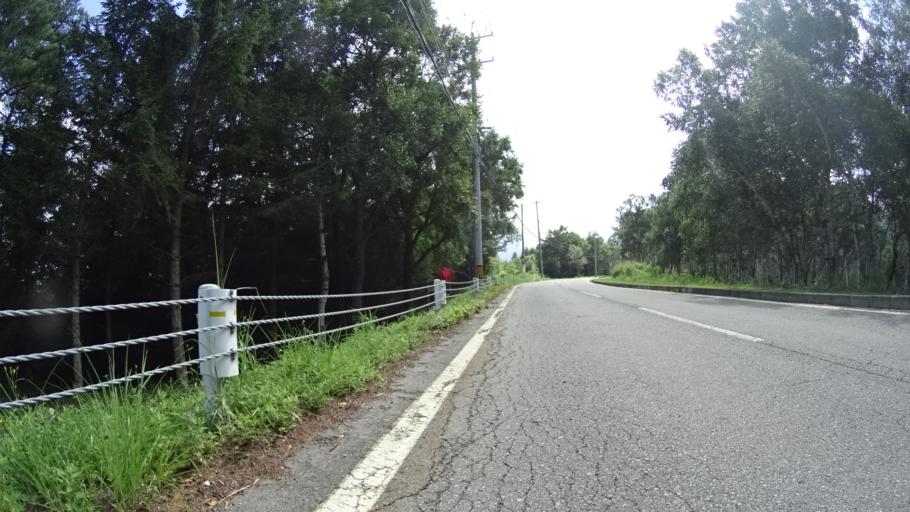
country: JP
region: Nagano
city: Saku
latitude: 36.0528
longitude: 138.4217
